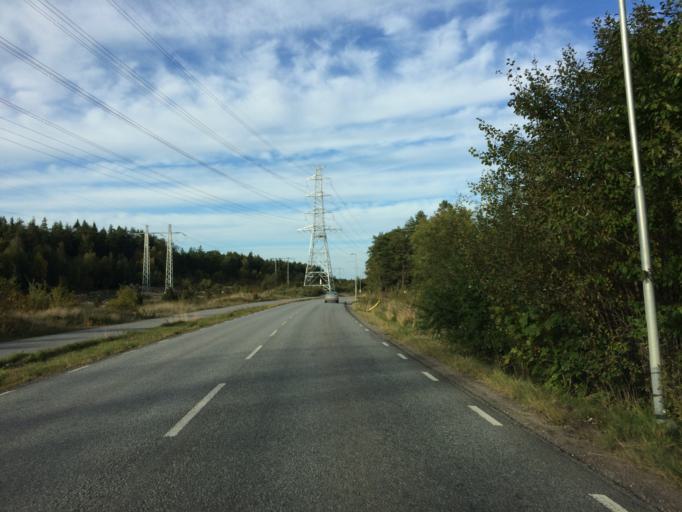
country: SE
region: Stockholm
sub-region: Sollentuna Kommun
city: Sollentuna
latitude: 59.4273
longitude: 17.9175
